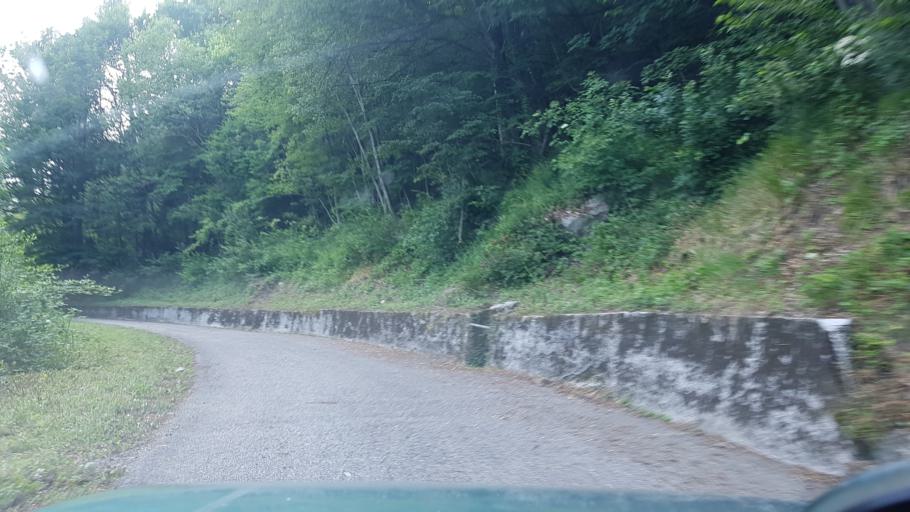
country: IT
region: Friuli Venezia Giulia
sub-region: Provincia di Udine
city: Torreano
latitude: 46.1772
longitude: 13.4183
